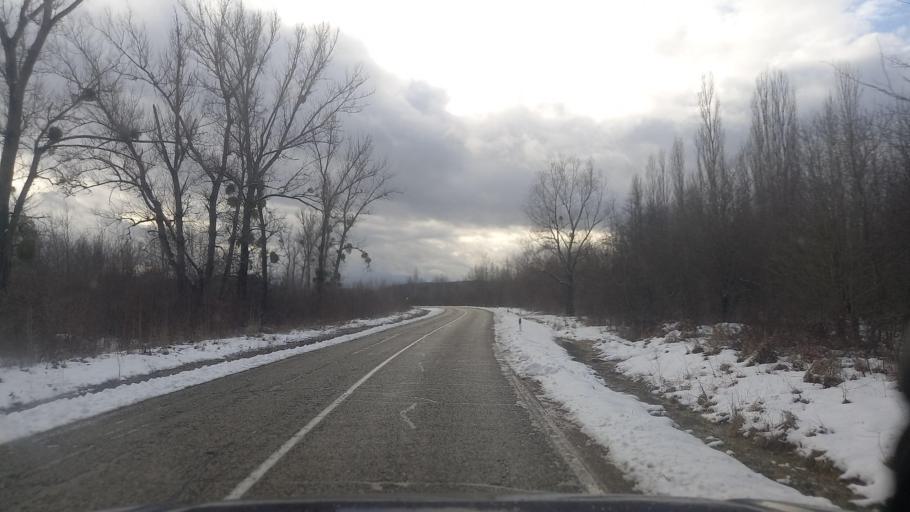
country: RU
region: Krasnodarskiy
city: Smolenskaya
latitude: 44.7567
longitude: 38.8459
